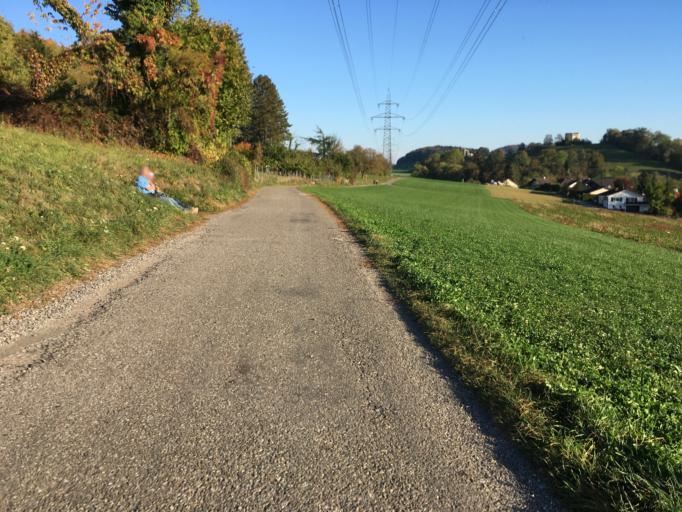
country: CH
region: Zurich
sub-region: Bezirk Buelach
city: Freienstein
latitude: 47.5386
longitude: 8.5811
